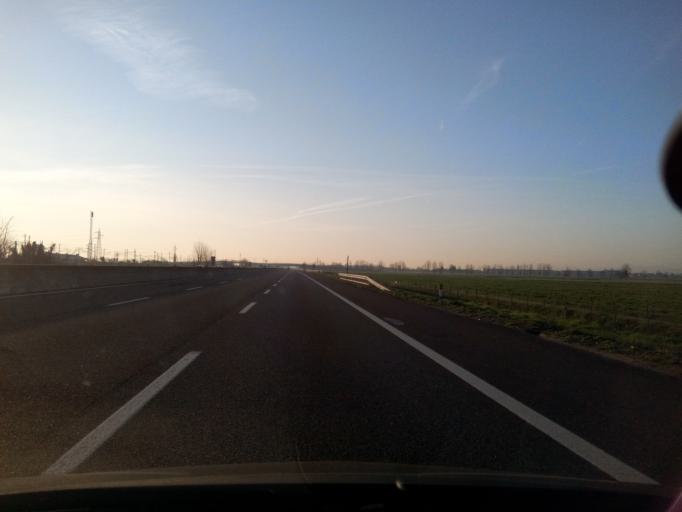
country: IT
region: Lombardy
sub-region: Provincia di Lodi
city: Ospedaletto Lodigiano
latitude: 45.1858
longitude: 9.5702
